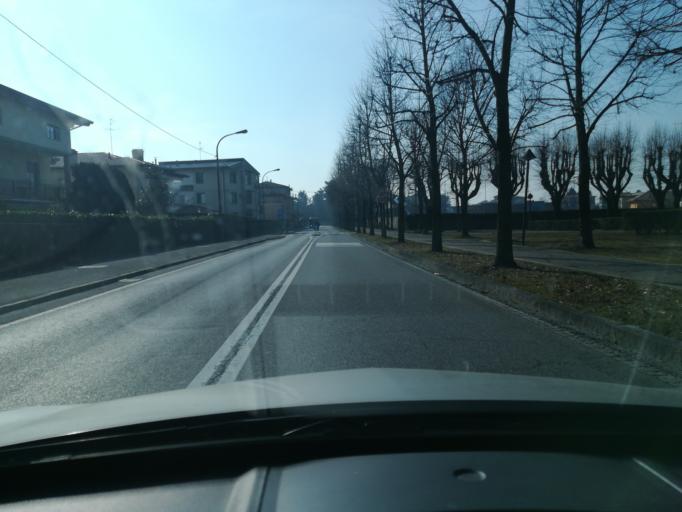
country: IT
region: Lombardy
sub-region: Provincia di Bergamo
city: Stezzano
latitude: 45.6550
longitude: 9.6553
